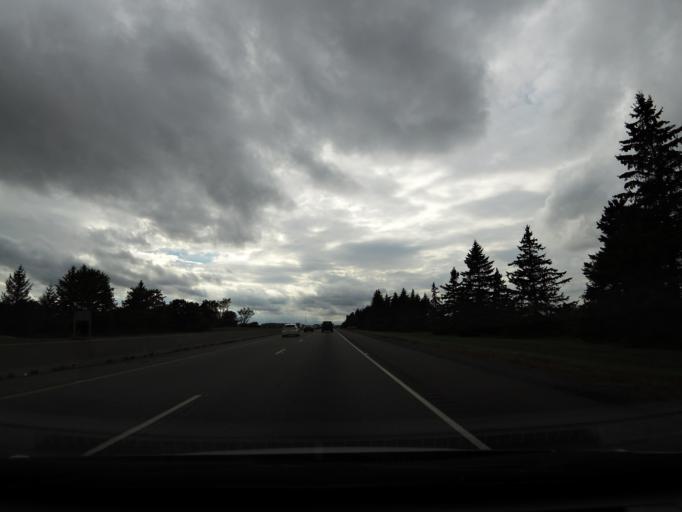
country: CA
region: Ontario
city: Kingston
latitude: 44.3053
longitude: -76.4049
